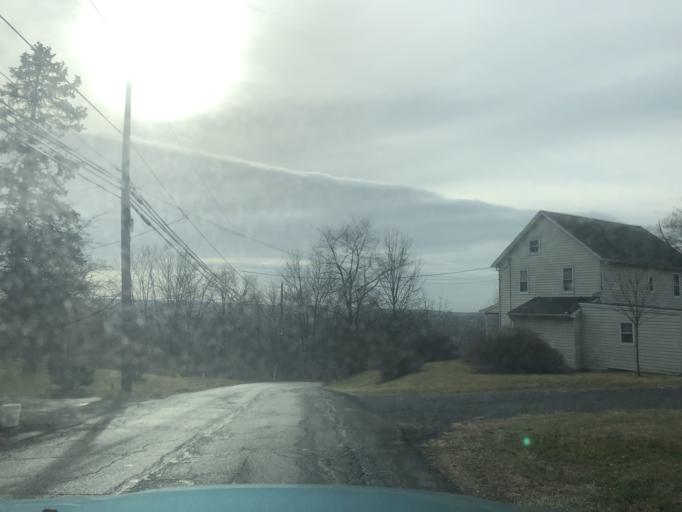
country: US
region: Pennsylvania
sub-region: Bucks County
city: Perkasie
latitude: 40.3821
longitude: -75.2919
